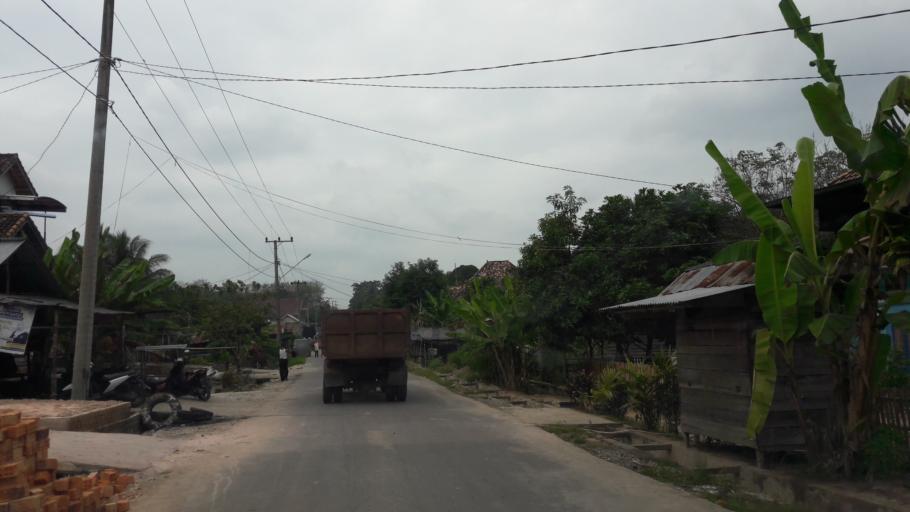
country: ID
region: South Sumatra
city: Gunungmenang
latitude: -3.2133
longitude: 103.9840
